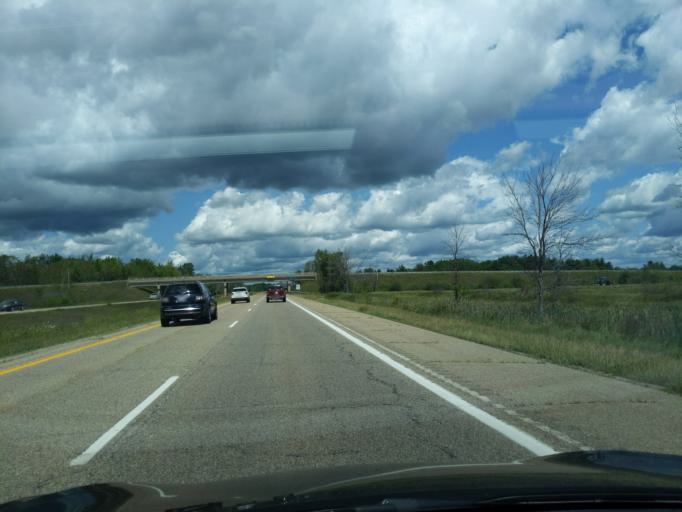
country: US
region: Michigan
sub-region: Roscommon County
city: Houghton Lake
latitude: 44.3700
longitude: -84.8078
